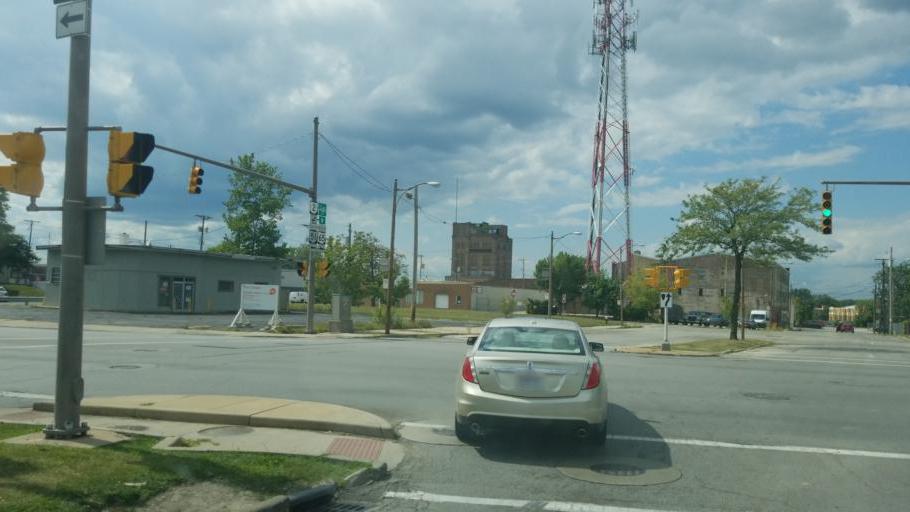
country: US
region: Ohio
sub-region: Lucas County
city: Toledo
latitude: 41.6425
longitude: -83.5406
